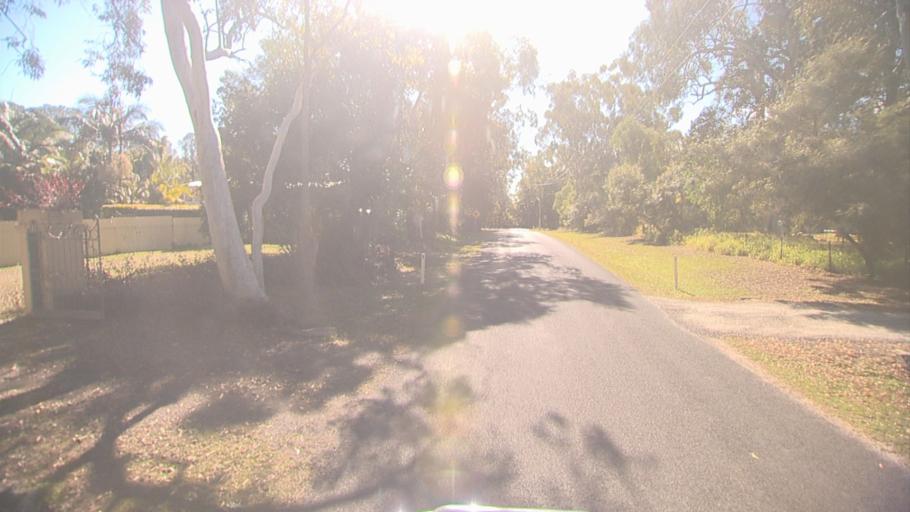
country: AU
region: Queensland
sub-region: Logan
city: Logan Reserve
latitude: -27.7407
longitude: 153.0944
